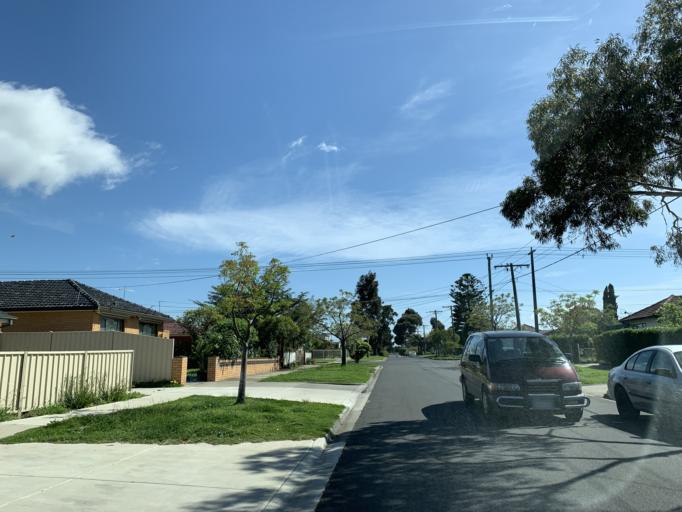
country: AU
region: Victoria
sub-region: Brimbank
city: Saint Albans
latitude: -37.7361
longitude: 144.7991
